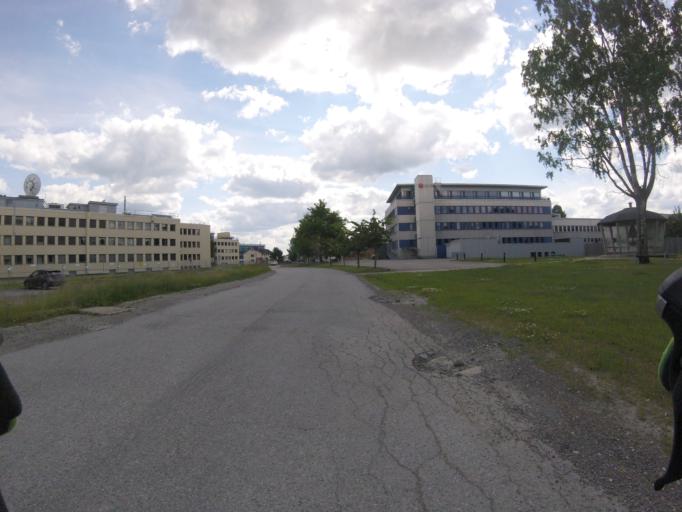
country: NO
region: Akershus
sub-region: Skedsmo
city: Lillestrom
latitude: 59.9758
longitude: 11.0454
